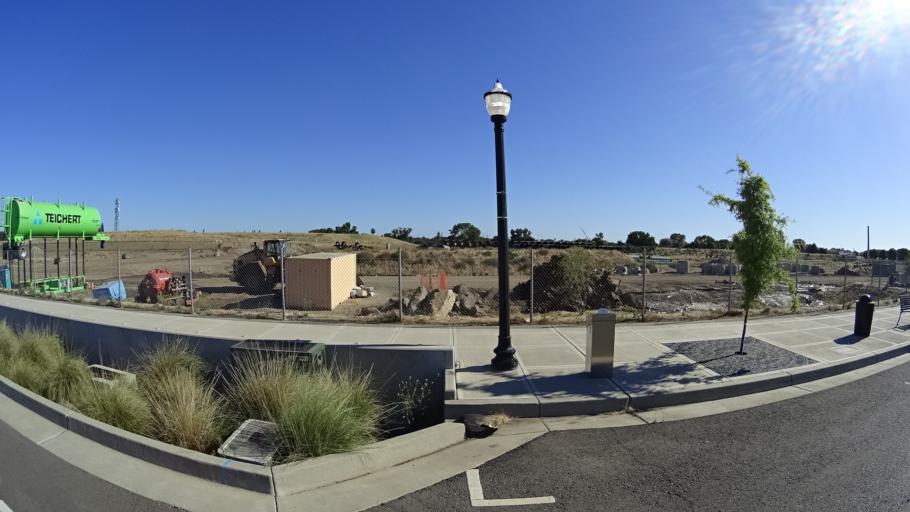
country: US
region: California
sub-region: Sacramento County
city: Sacramento
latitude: 38.5902
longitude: -121.4970
